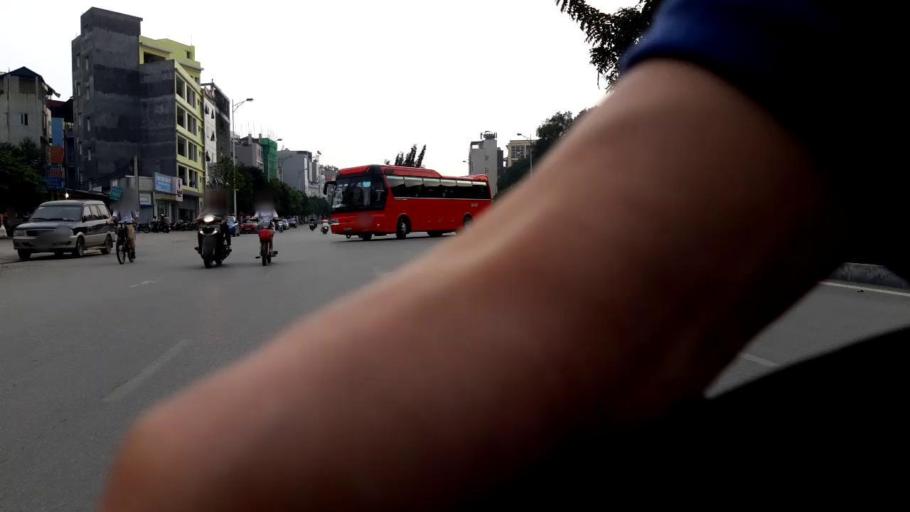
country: VN
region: Ha Noi
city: Cau Giay
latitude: 21.0381
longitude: 105.7979
